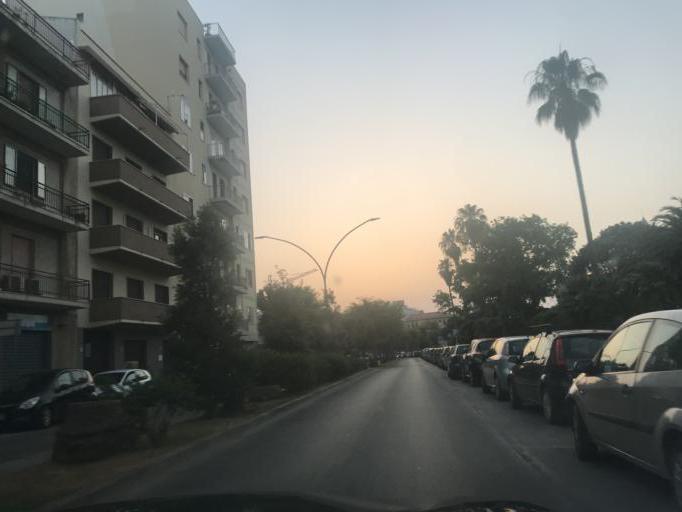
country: IT
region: Sardinia
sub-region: Provincia di Sassari
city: Alghero
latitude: 40.5551
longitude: 8.3200
